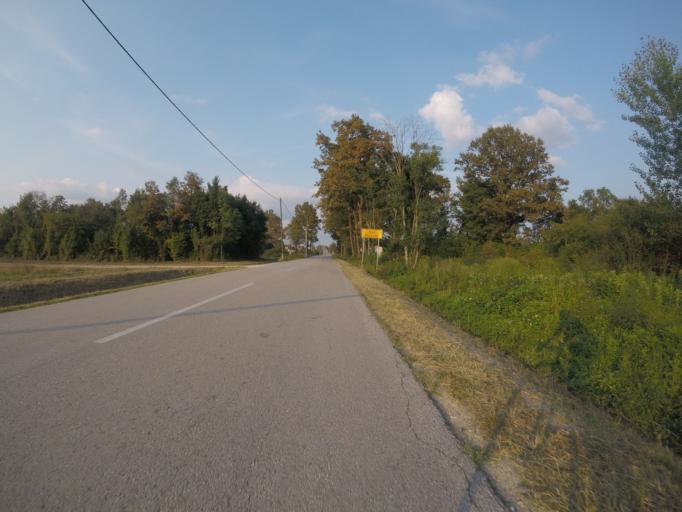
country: HR
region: Zagrebacka
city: Kuce
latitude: 45.7126
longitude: 16.1911
